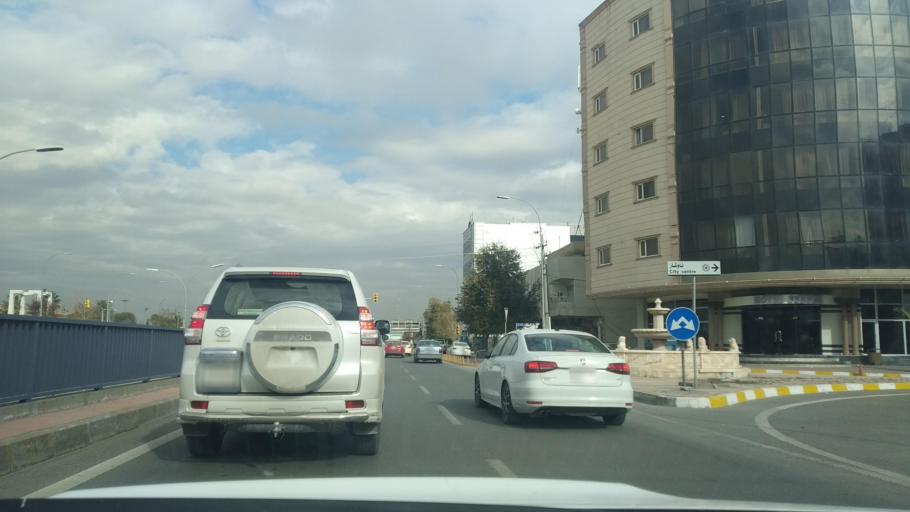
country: IQ
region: Arbil
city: Erbil
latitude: 36.1891
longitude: 43.9939
